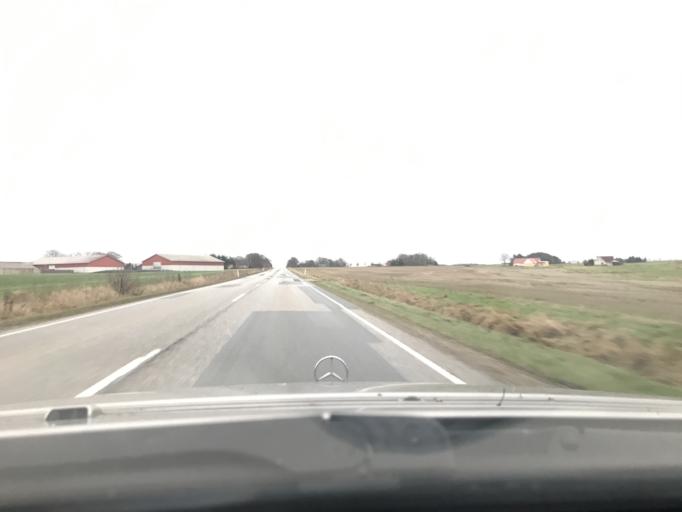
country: DK
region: South Denmark
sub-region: Tonder Kommune
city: Toftlund
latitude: 55.1589
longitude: 9.0859
